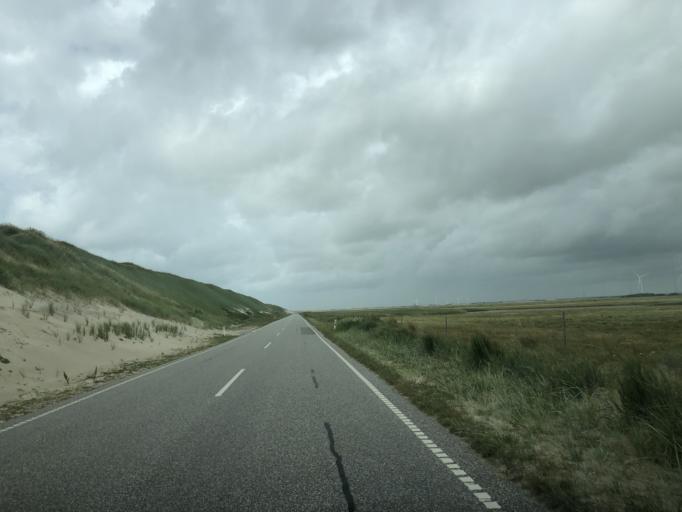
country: DK
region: Central Jutland
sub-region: Lemvig Kommune
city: Harboore
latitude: 56.4309
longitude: 8.1240
